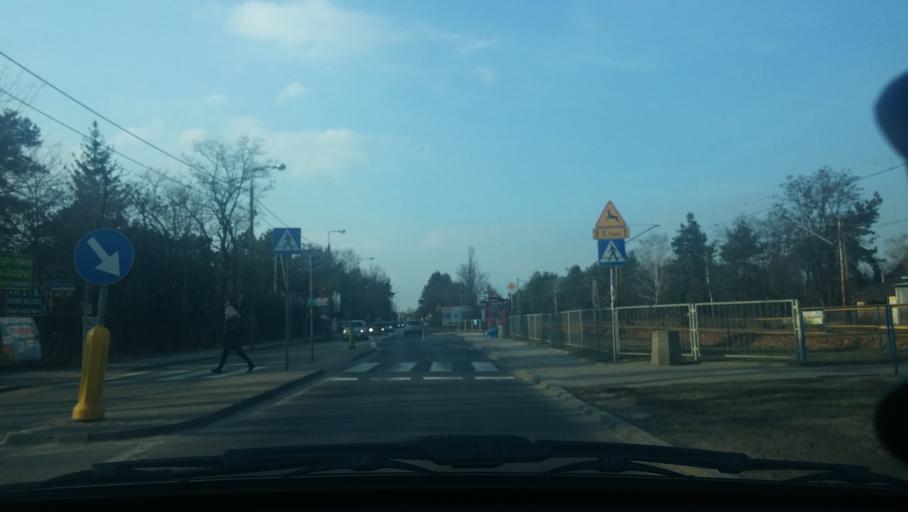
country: PL
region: Masovian Voivodeship
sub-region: Warszawa
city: Wawer
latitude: 52.1863
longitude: 21.1863
